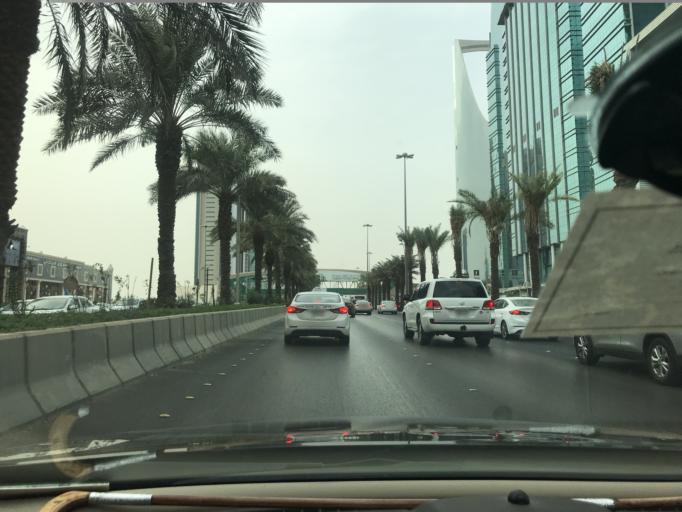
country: SA
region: Ar Riyad
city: Riyadh
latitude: 24.7059
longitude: 46.6753
